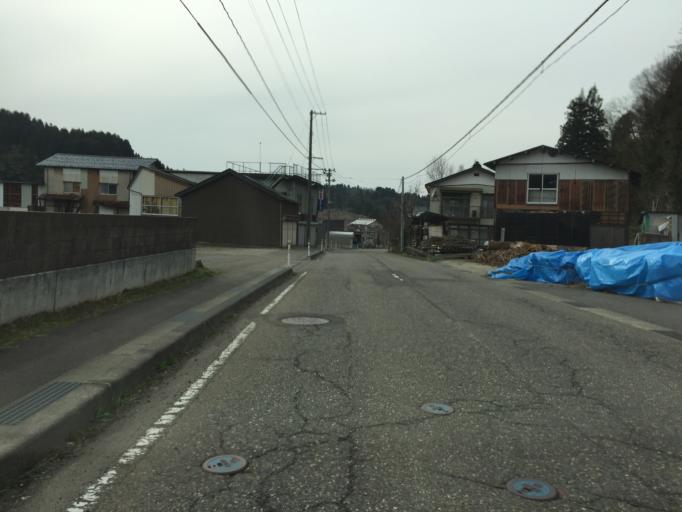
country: JP
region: Niigata
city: Tochio-honcho
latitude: 37.4484
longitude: 139.0175
